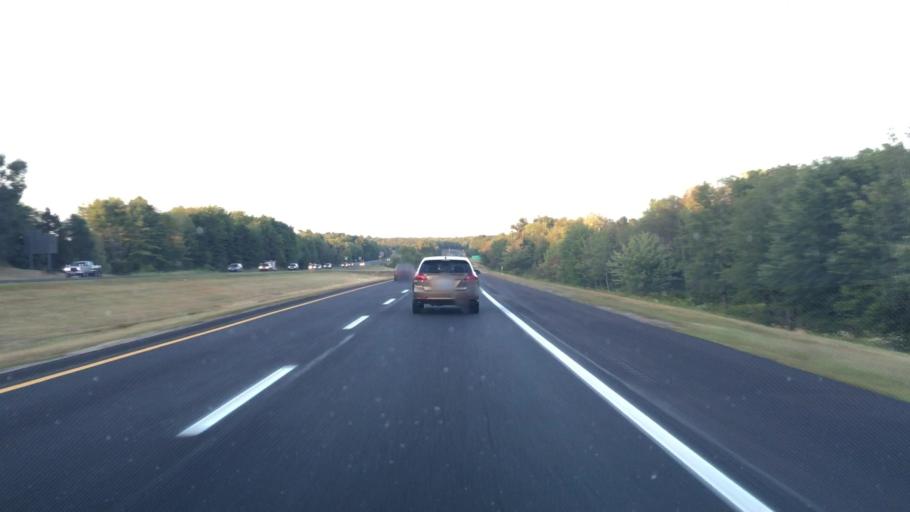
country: US
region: Maine
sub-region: Sagadahoc County
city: Topsham
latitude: 43.9495
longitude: -69.9708
